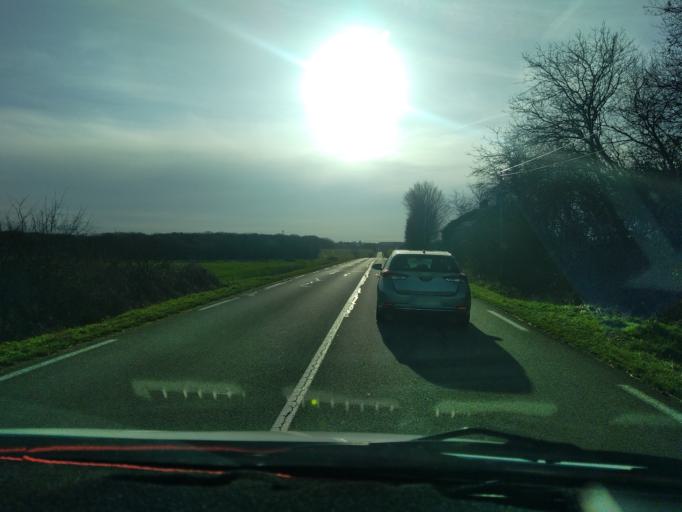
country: FR
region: Franche-Comte
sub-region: Departement de la Haute-Saone
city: Gray
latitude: 47.3727
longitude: 5.6653
